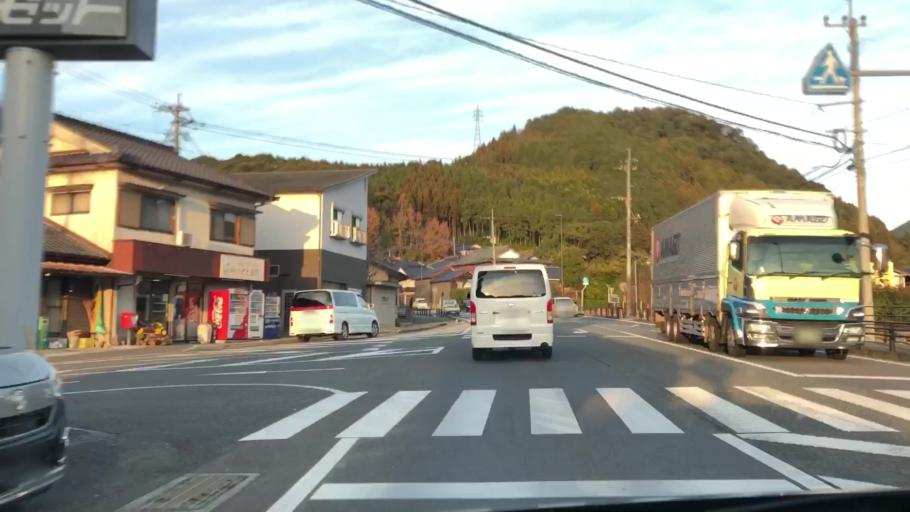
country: JP
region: Kumamoto
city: Minamata
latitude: 32.2340
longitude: 130.4646
